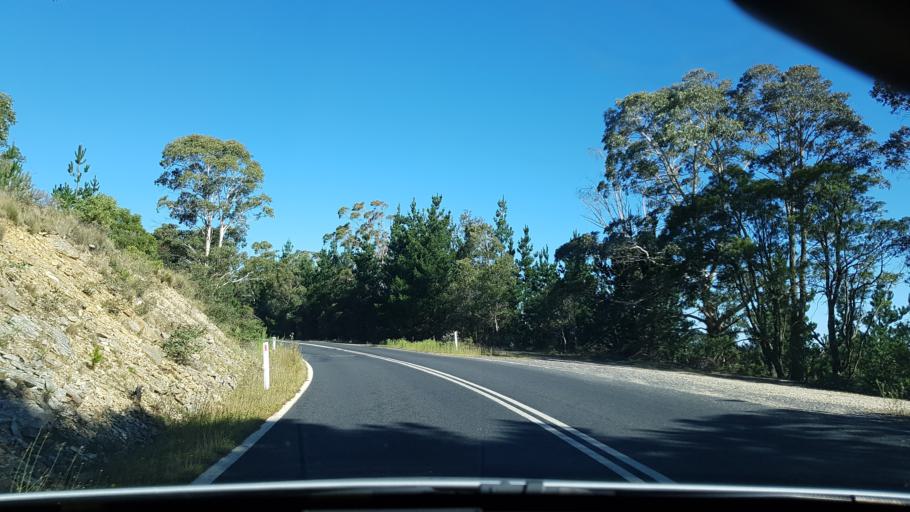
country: AU
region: New South Wales
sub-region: Oberon
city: Oberon
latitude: -33.7231
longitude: 150.0479
